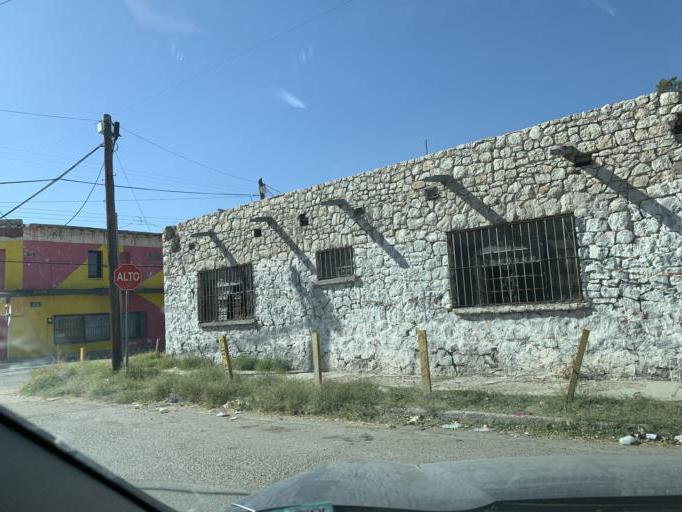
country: MX
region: Chihuahua
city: Ciudad Juarez
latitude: 31.7271
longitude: -106.4599
